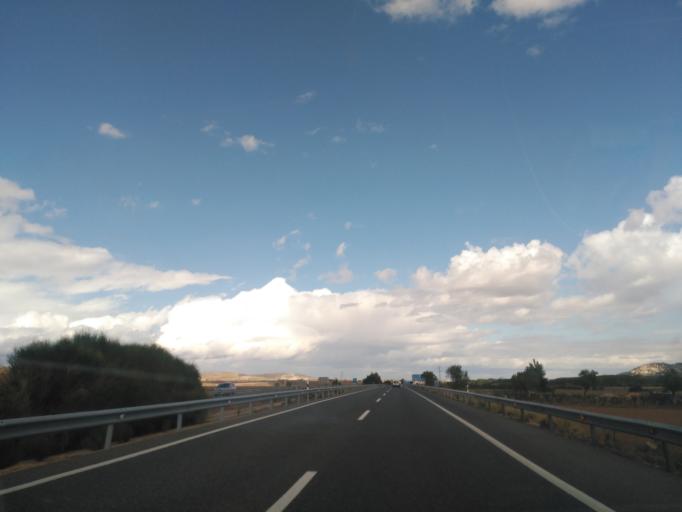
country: ES
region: Castille and Leon
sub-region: Provincia de Burgos
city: Villaquiran de los Infantes
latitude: 42.2279
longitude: -3.9939
